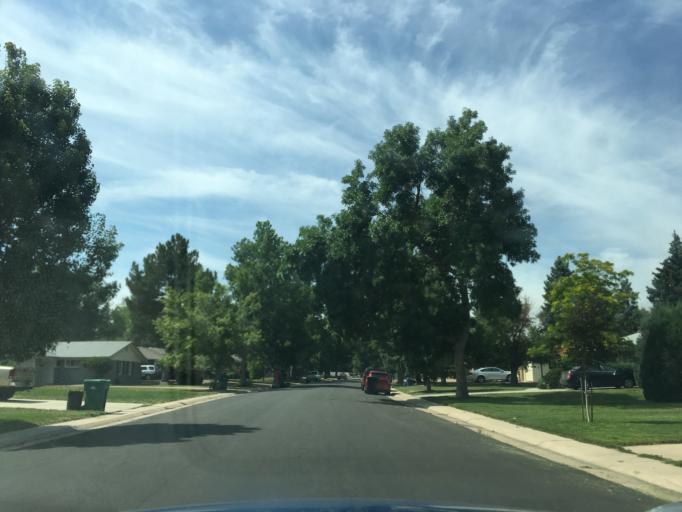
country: US
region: Colorado
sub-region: Adams County
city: Aurora
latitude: 39.7213
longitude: -104.8597
